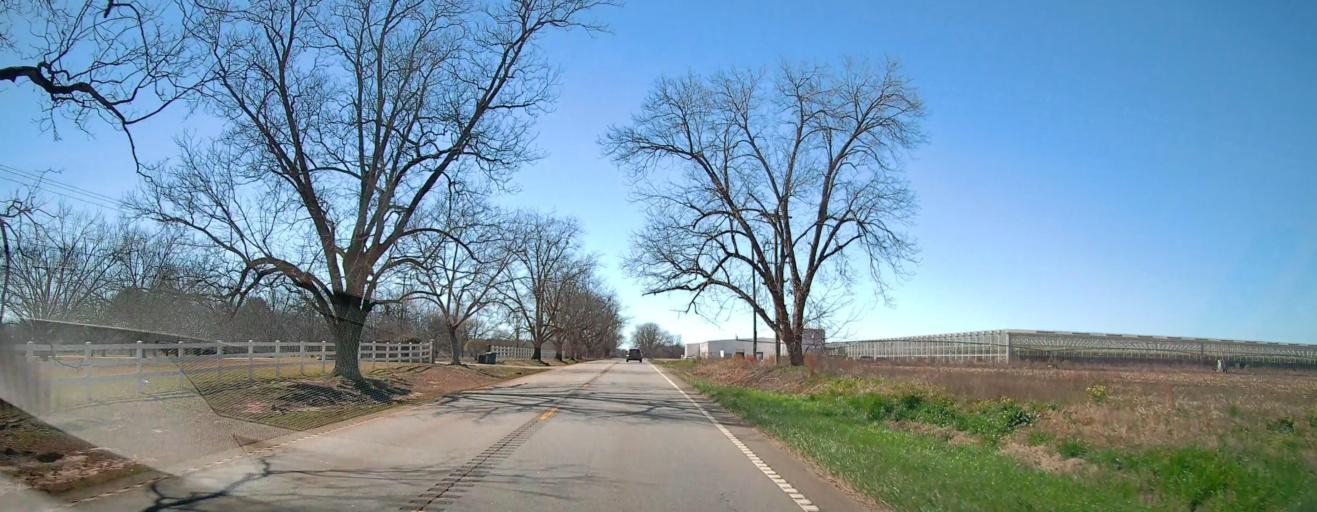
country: US
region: Georgia
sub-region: Peach County
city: Fort Valley
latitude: 32.5540
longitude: -83.8100
